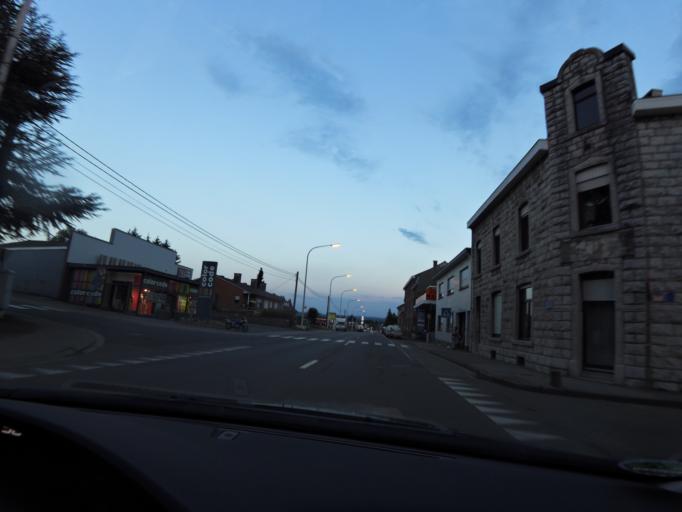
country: BE
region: Wallonia
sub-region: Province de Liege
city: Welkenraedt
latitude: 50.6545
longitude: 5.9929
